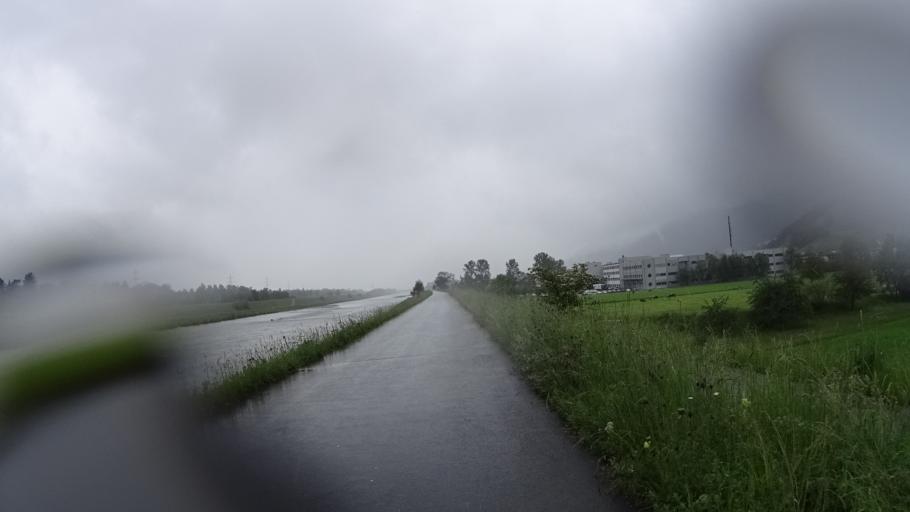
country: LI
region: Triesen
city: Triesen
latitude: 47.1053
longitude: 9.5199
